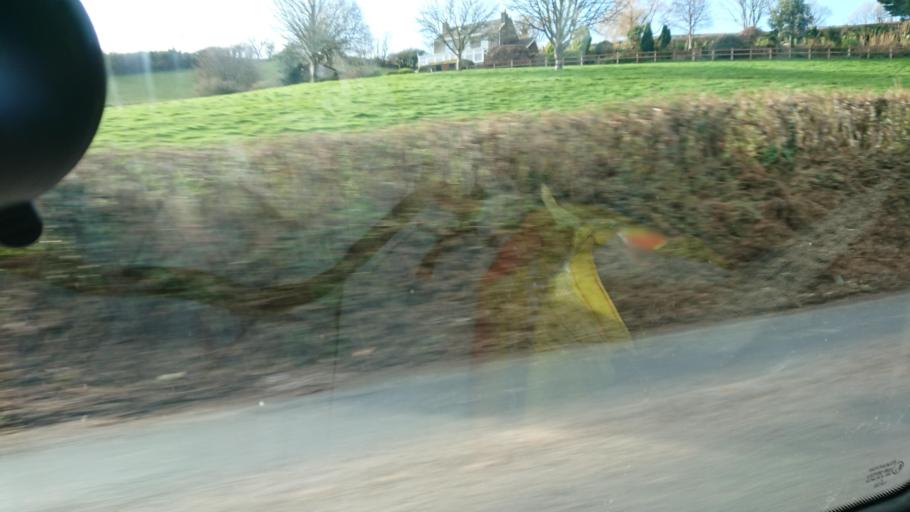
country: GB
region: England
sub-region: Devon
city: Modbury
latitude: 50.3279
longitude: -3.8426
